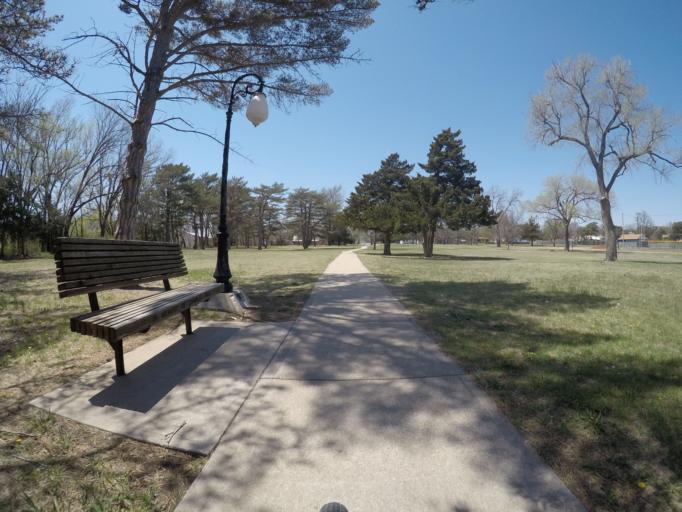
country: US
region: Kansas
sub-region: Pratt County
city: Pratt
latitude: 37.6376
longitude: -98.7331
